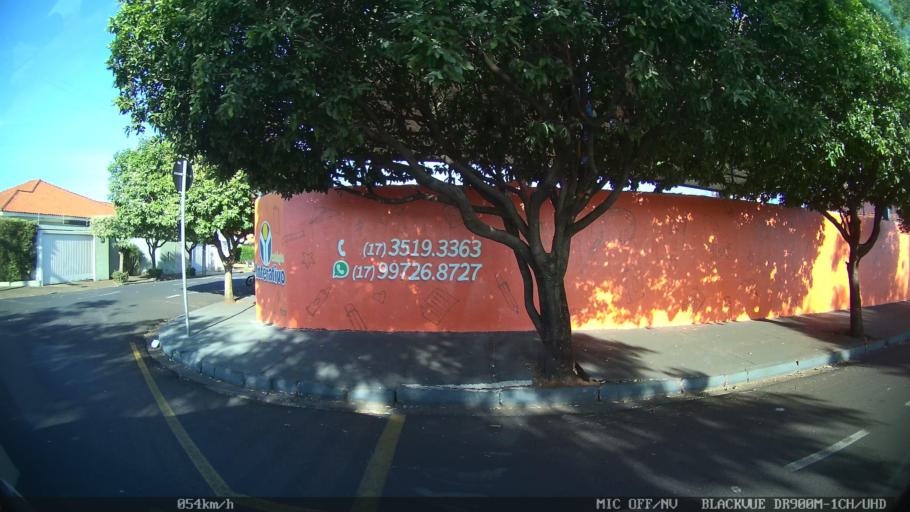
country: BR
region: Sao Paulo
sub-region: Sao Jose Do Rio Preto
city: Sao Jose do Rio Preto
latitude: -20.8152
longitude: -49.4018
